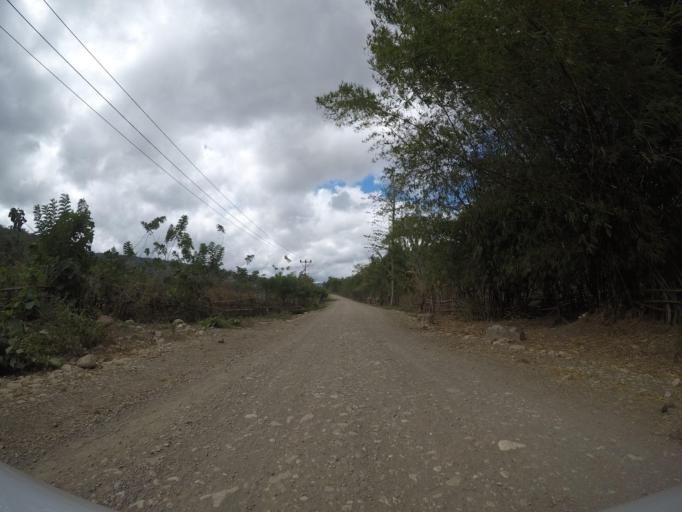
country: TL
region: Lautem
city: Lospalos
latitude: -8.4986
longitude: 126.8274
